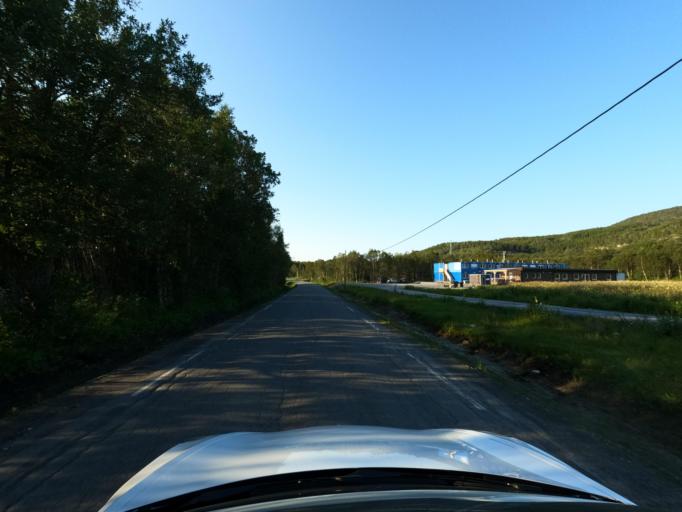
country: NO
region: Troms
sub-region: Skanland
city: Evenskjer
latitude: 68.4722
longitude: 16.7046
